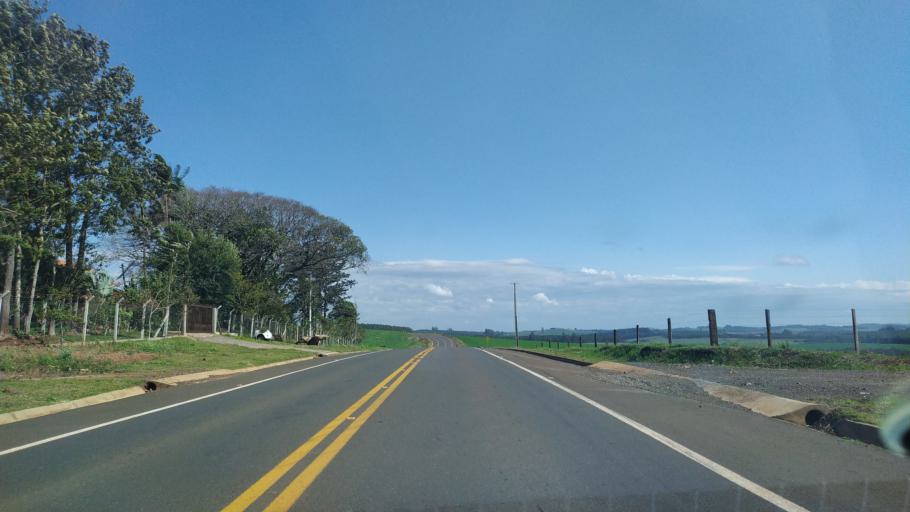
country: BR
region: Parana
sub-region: Ortigueira
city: Ortigueira
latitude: -24.2565
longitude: -50.8054
